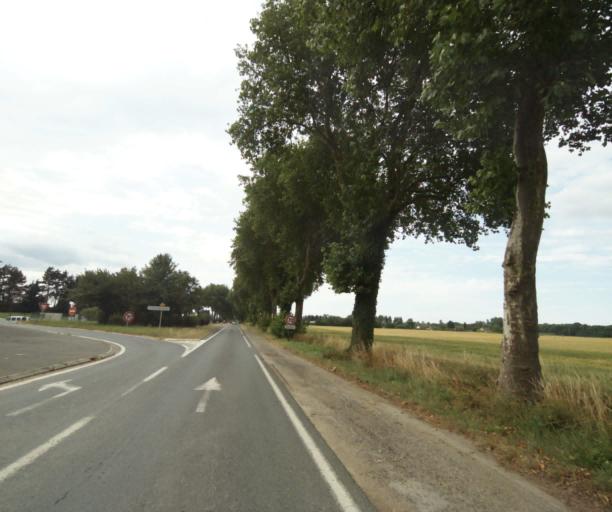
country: FR
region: Ile-de-France
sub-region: Departement de Seine-et-Marne
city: Chailly-en-Biere
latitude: 48.4570
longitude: 2.6155
